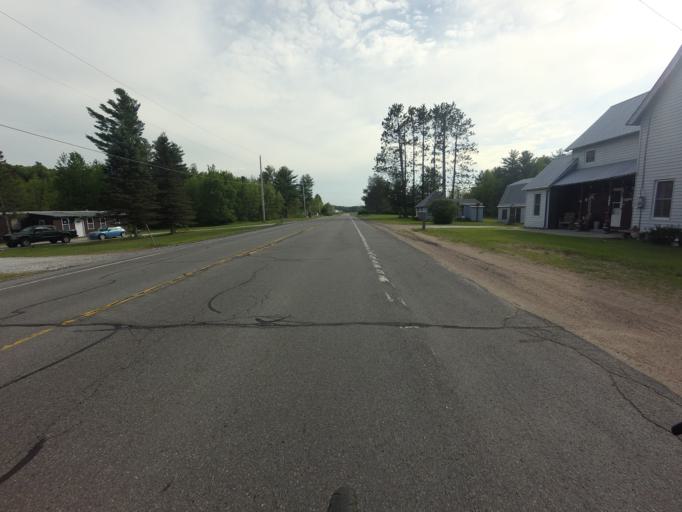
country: US
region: New York
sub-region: St. Lawrence County
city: Gouverneur
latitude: 44.1732
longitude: -75.2964
